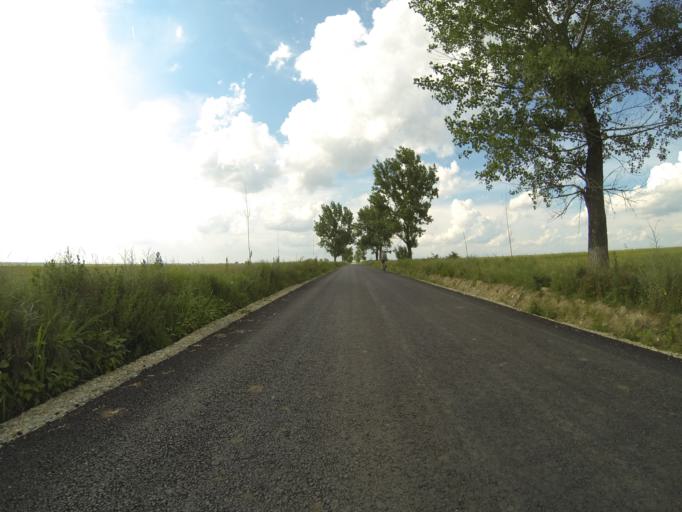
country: RO
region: Dolj
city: Satu Nou Calopar
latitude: 44.1378
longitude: 23.7950
